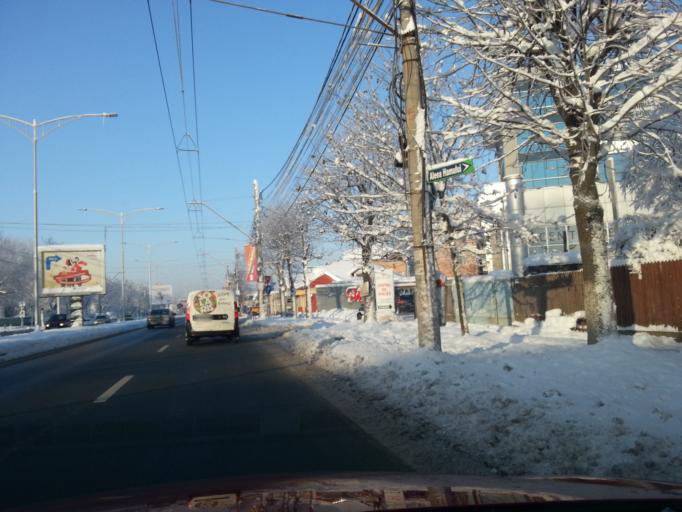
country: RO
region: Ilfov
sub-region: Comuna Chiajna
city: Rosu
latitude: 44.4343
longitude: 25.9913
